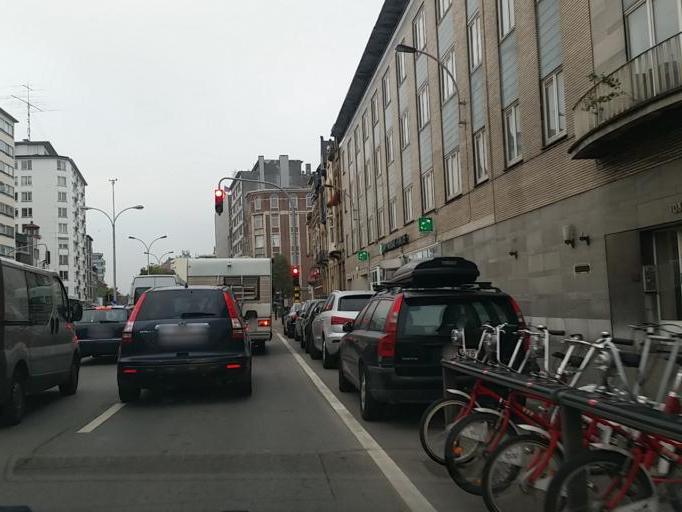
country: BE
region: Flanders
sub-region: Provincie Antwerpen
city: Antwerpen
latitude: 51.2100
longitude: 4.4277
